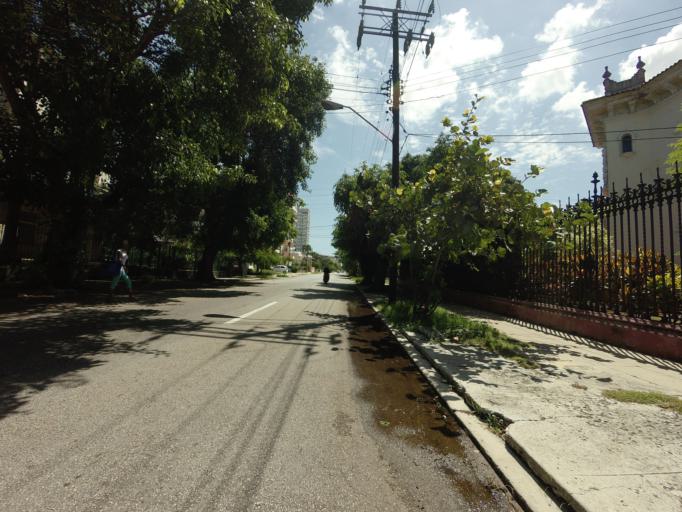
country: CU
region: La Habana
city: Havana
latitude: 23.1364
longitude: -82.4024
